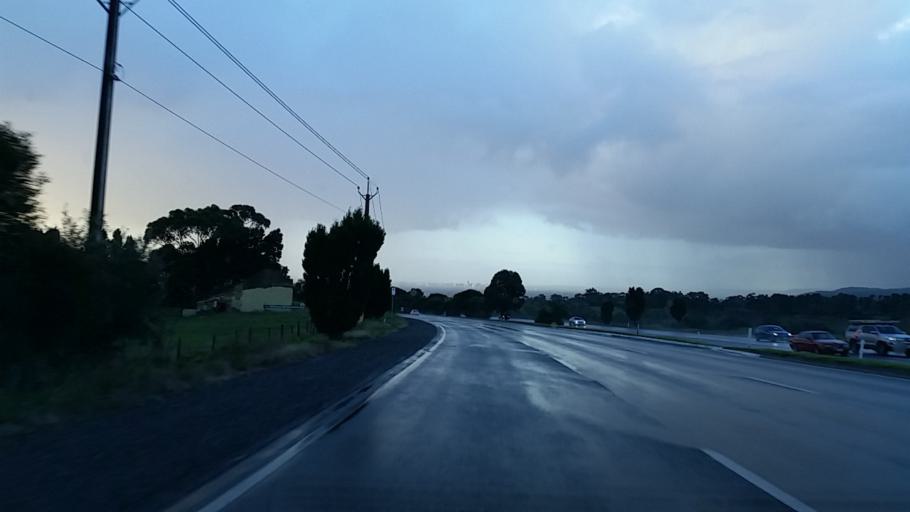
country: AU
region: South Australia
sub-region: Onkaparinga
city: Bedford Park
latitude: -35.0464
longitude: 138.5605
